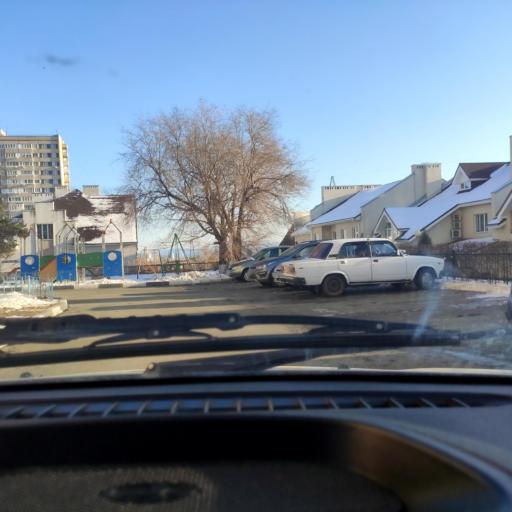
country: RU
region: Samara
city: Zhigulevsk
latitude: 53.4733
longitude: 49.4659
